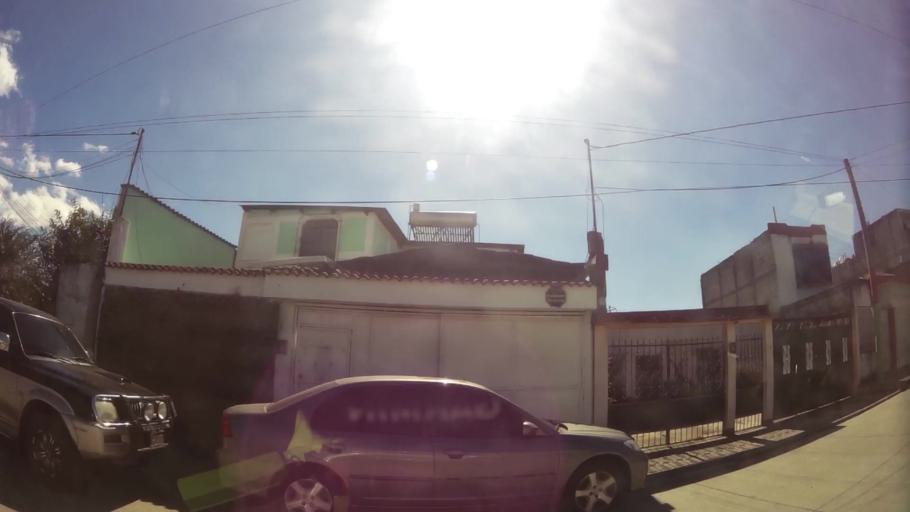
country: GT
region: Guatemala
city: Petapa
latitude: 14.5068
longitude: -90.5642
